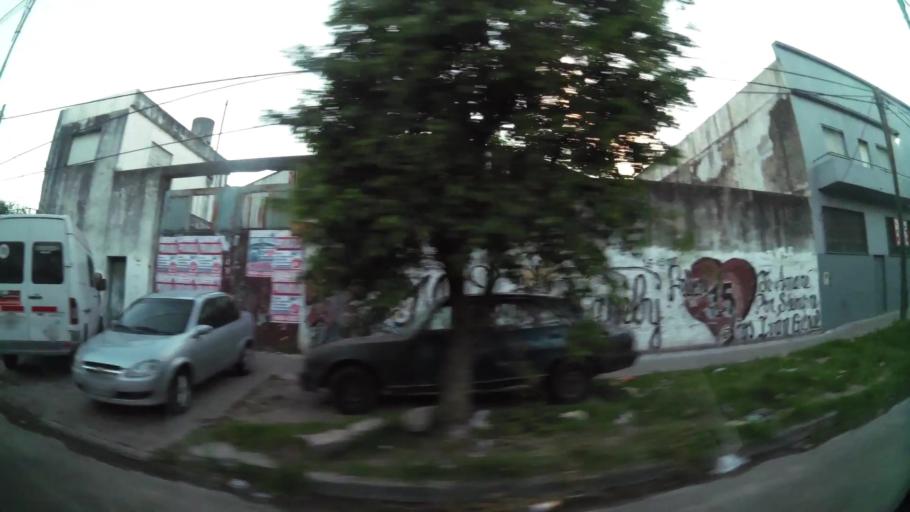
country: AR
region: Buenos Aires F.D.
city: Villa Lugano
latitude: -34.6792
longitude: -58.4687
